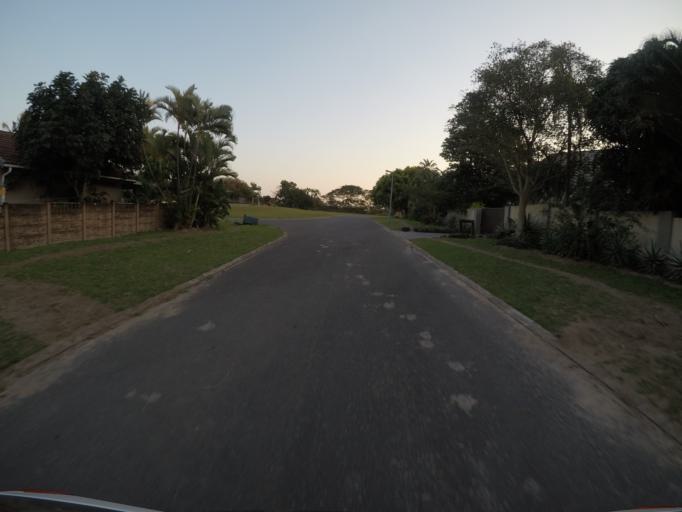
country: ZA
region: KwaZulu-Natal
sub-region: uThungulu District Municipality
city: Richards Bay
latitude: -28.7682
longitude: 32.1246
